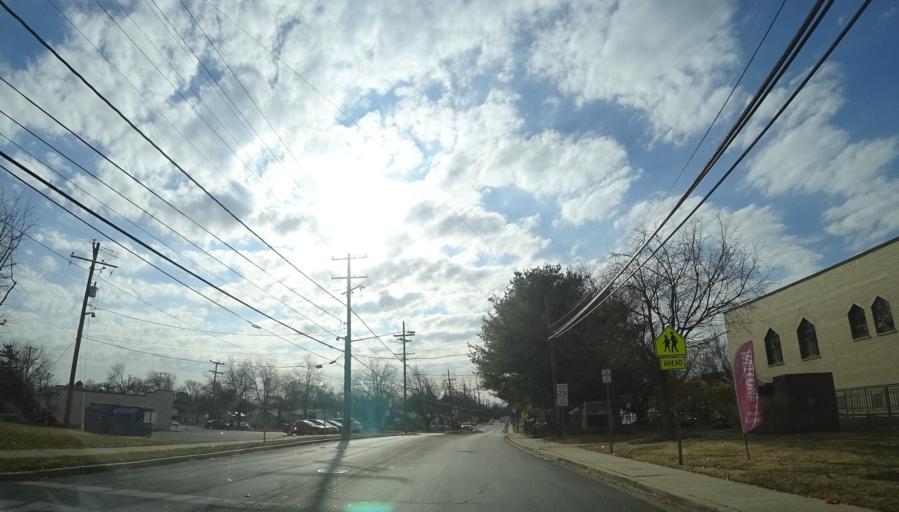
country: US
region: Maryland
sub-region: Montgomery County
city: Rockville
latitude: 39.0931
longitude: -77.1437
